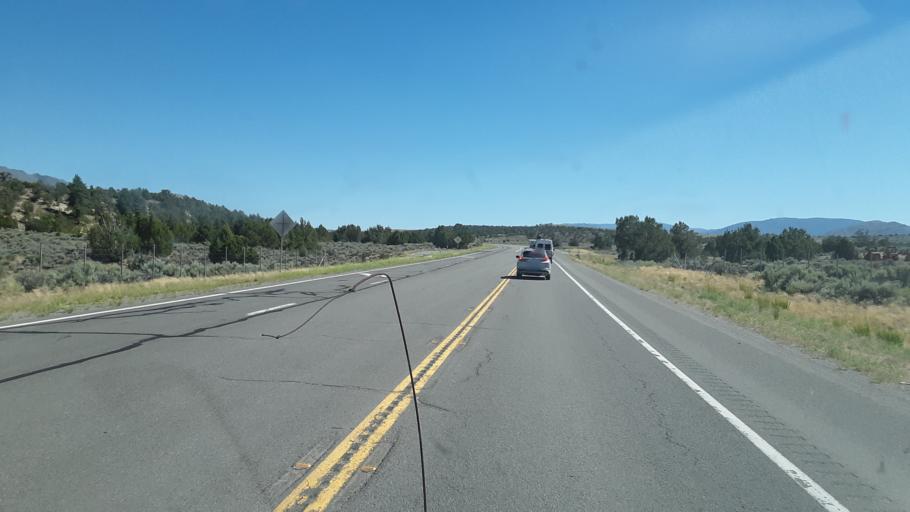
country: US
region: Nevada
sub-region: Washoe County
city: Cold Springs
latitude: 39.8536
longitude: -120.0438
